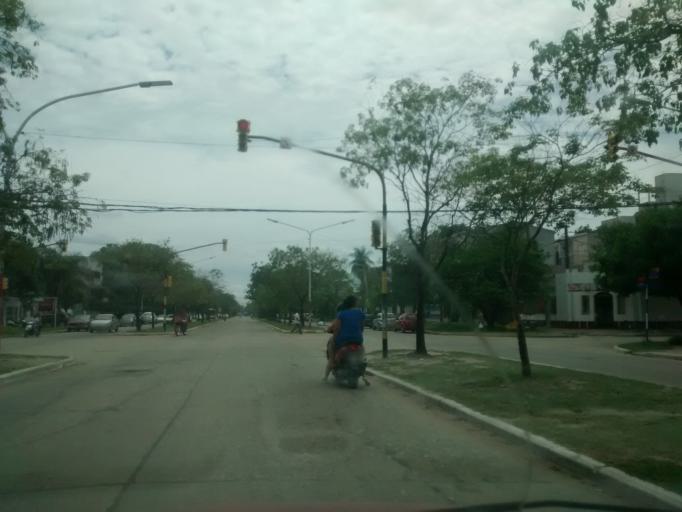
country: AR
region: Chaco
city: Resistencia
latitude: -27.4608
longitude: -58.9831
